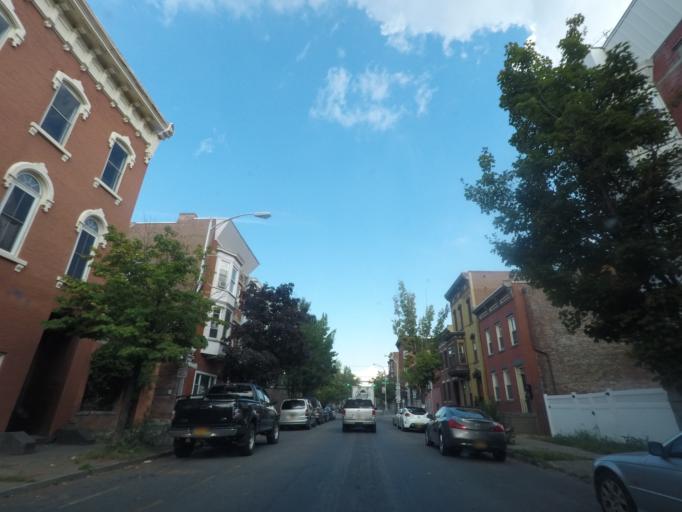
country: US
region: New York
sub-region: Rensselaer County
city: Troy
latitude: 42.7269
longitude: -73.6900
